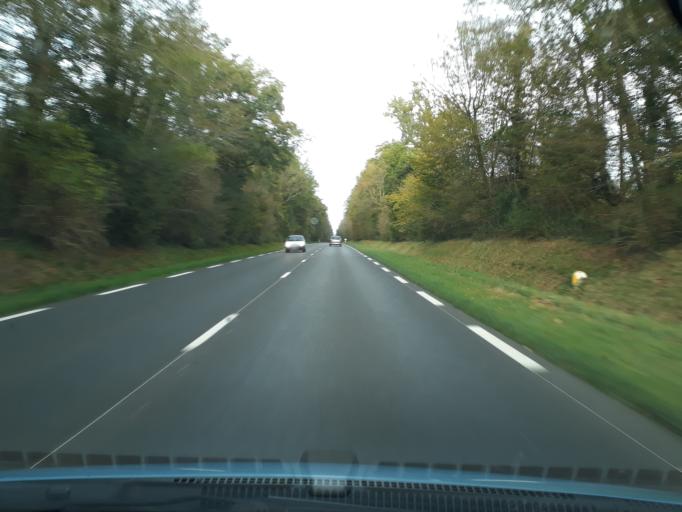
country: FR
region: Ile-de-France
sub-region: Departement de Seine-et-Marne
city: Acheres-la-Foret
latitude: 48.3535
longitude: 2.6162
